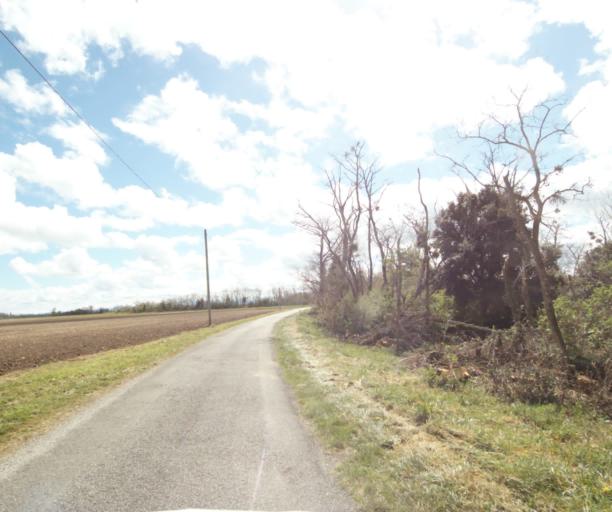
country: FR
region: Midi-Pyrenees
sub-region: Departement de l'Ariege
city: Saverdun
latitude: 43.2706
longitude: 1.5825
